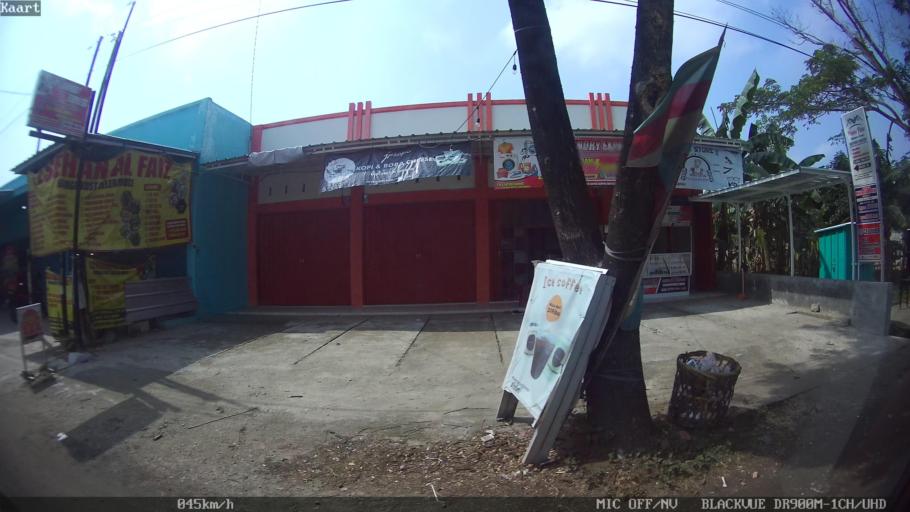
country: ID
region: Lampung
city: Gadingrejo
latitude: -5.3748
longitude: 105.0410
